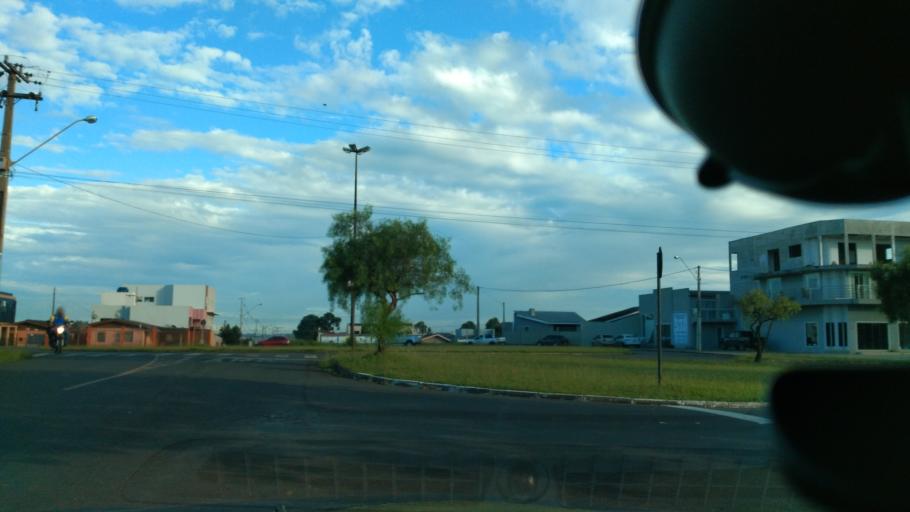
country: BR
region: Parana
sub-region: Guarapuava
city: Guarapuava
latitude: -25.3780
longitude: -51.4791
